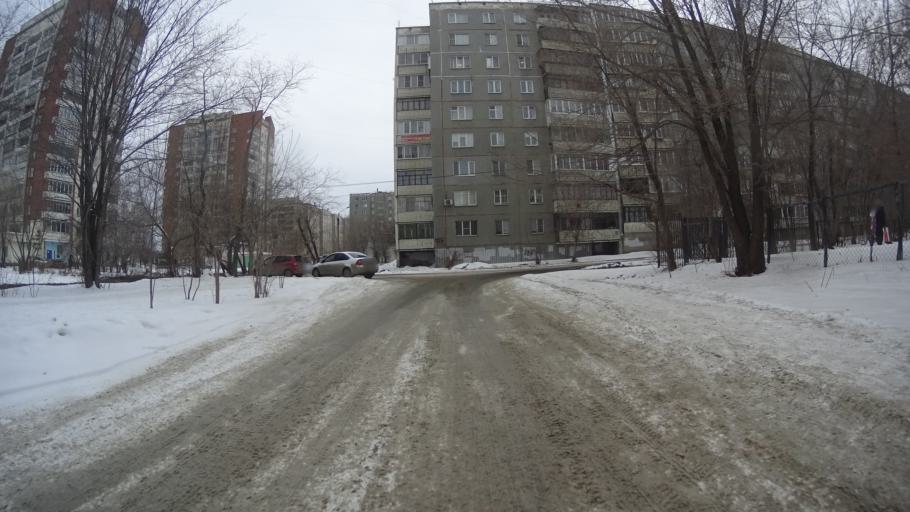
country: RU
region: Chelyabinsk
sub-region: Gorod Chelyabinsk
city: Chelyabinsk
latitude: 55.1757
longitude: 61.3418
